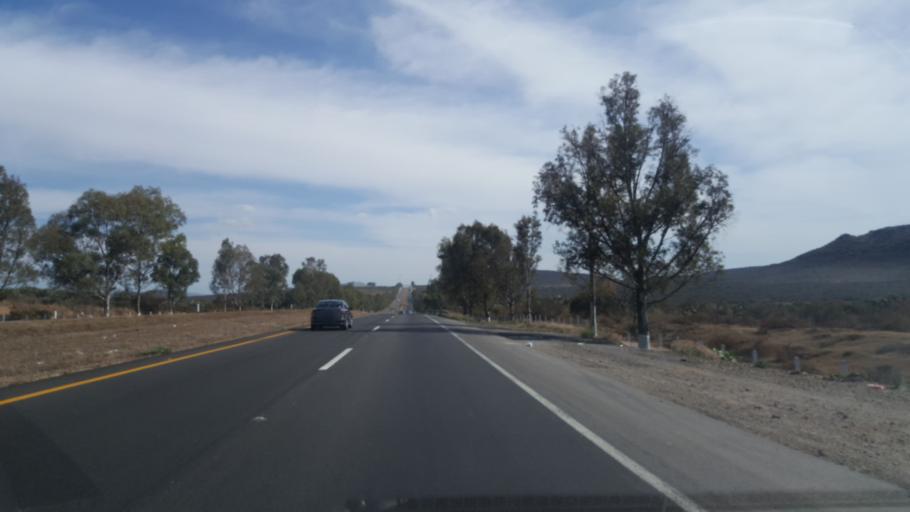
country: MX
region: Jalisco
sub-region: Lagos de Moreno
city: Cristeros [Fraccionamiento]
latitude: 21.2753
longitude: -101.9827
